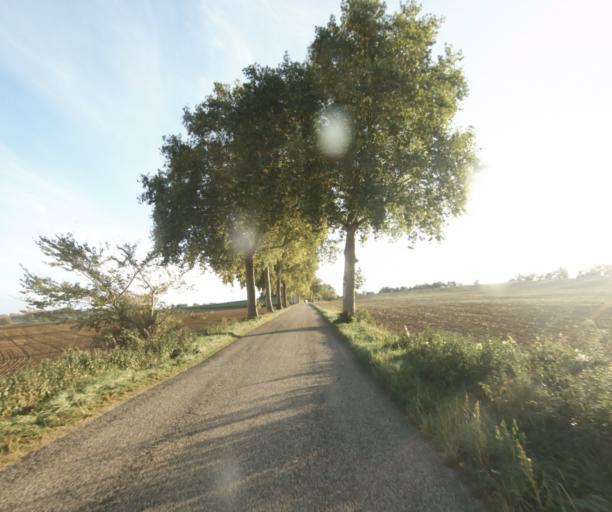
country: FR
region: Midi-Pyrenees
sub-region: Departement du Gers
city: Gondrin
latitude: 43.8811
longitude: 0.2882
